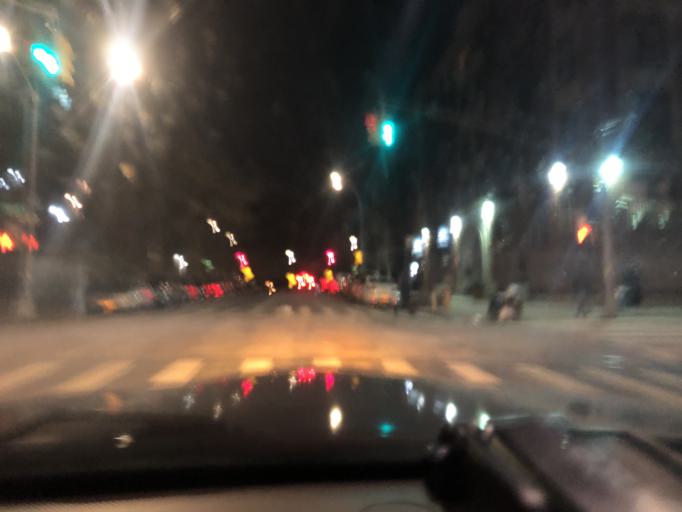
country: US
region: New York
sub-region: New York County
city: Inwood
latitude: 40.8683
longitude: -73.9216
